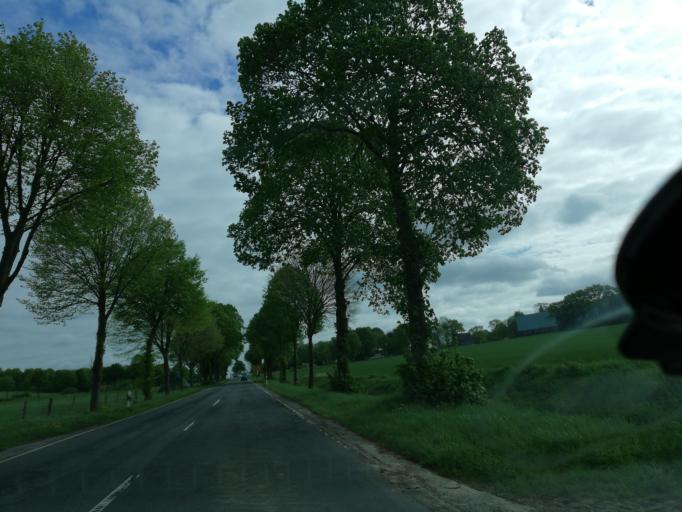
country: DE
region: North Rhine-Westphalia
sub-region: Regierungsbezirk Arnsberg
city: Schwelm
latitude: 51.3042
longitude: 7.2752
